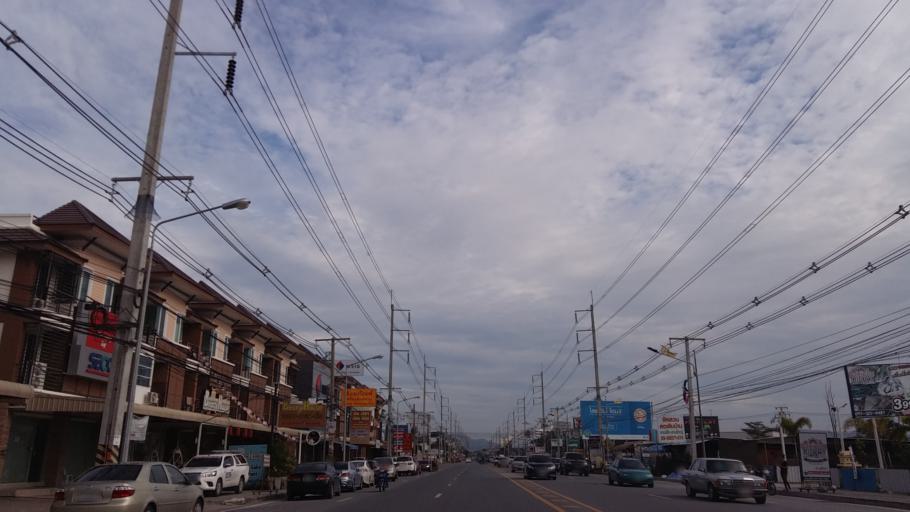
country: TH
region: Chon Buri
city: Chon Buri
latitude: 13.3251
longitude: 100.9423
